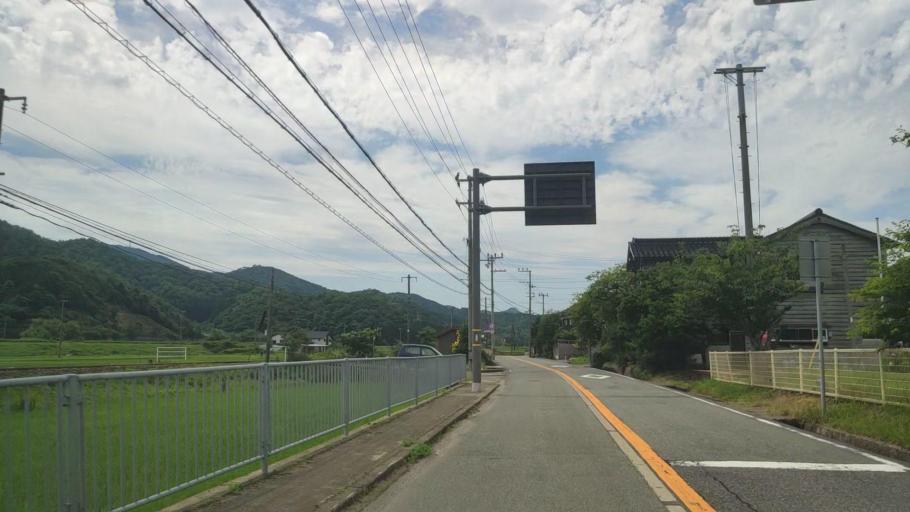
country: JP
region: Hyogo
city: Toyooka
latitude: 35.6432
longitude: 134.7581
